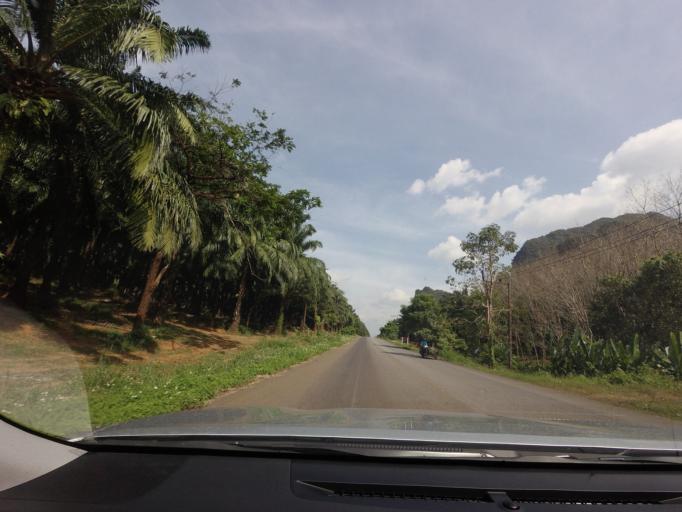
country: TH
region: Phangnga
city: Ban Ao Nang
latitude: 8.1463
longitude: 98.8153
